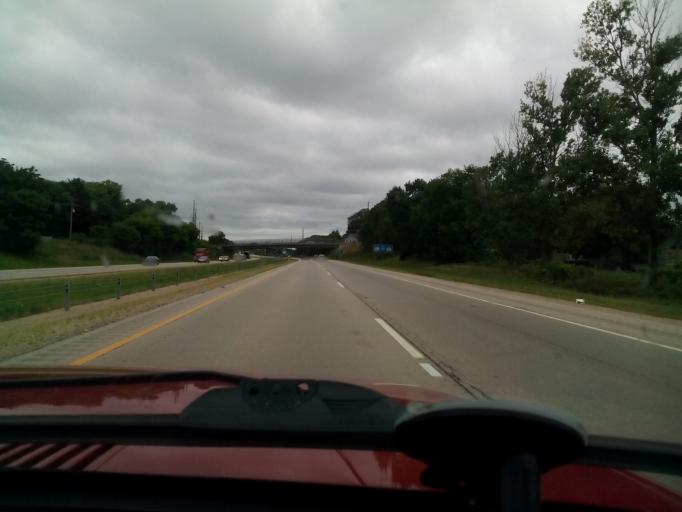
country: US
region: Wisconsin
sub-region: Dane County
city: Sun Prairie
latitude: 43.1932
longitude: -89.2225
